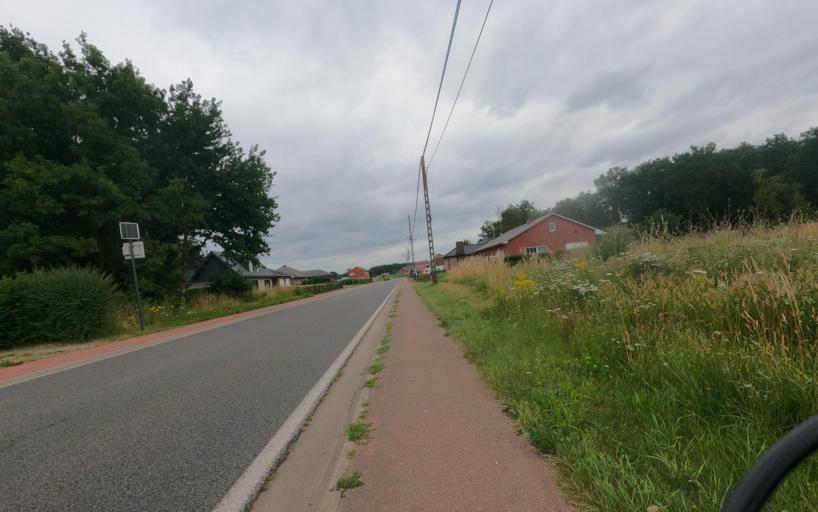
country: BE
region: Flanders
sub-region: Provincie Vlaams-Brabant
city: Tremelo
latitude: 50.9759
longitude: 4.7266
